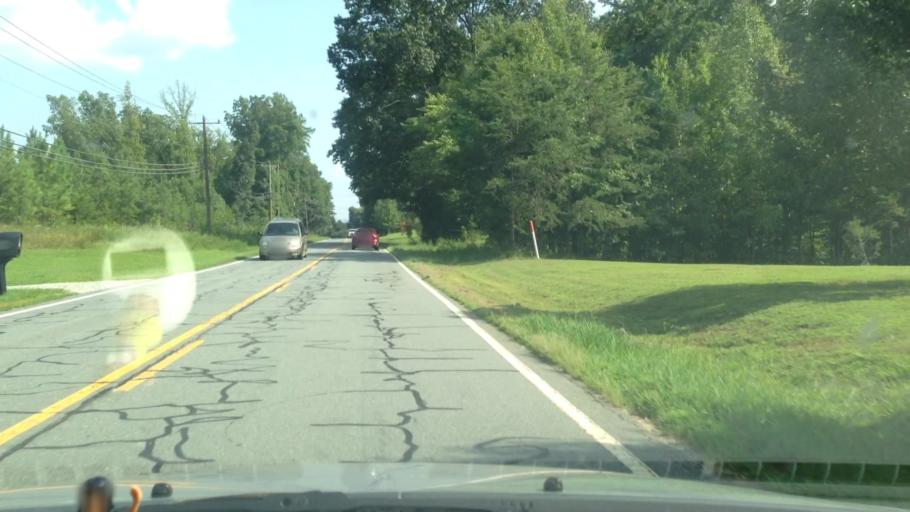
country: US
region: North Carolina
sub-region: Forsyth County
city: Kernersville
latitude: 36.1717
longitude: -80.0581
